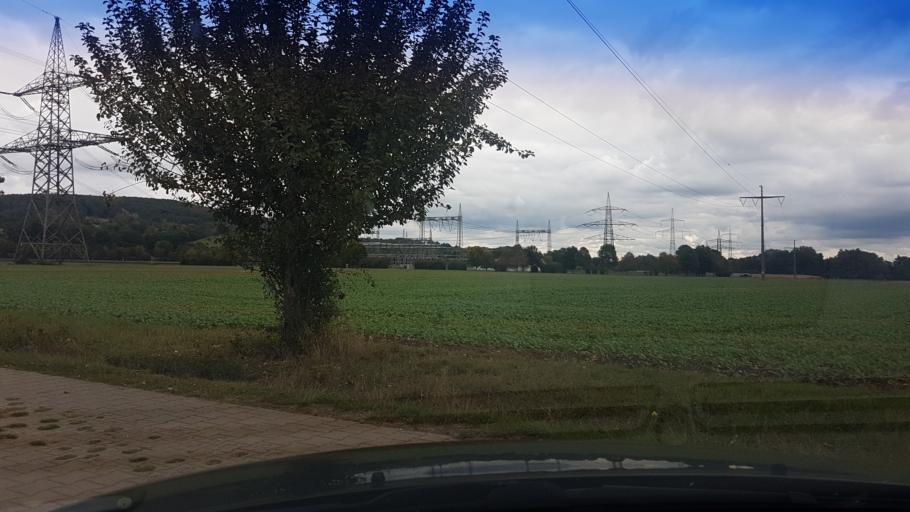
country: DE
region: Bavaria
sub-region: Upper Franconia
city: Bischberg
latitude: 49.9265
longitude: 10.8319
